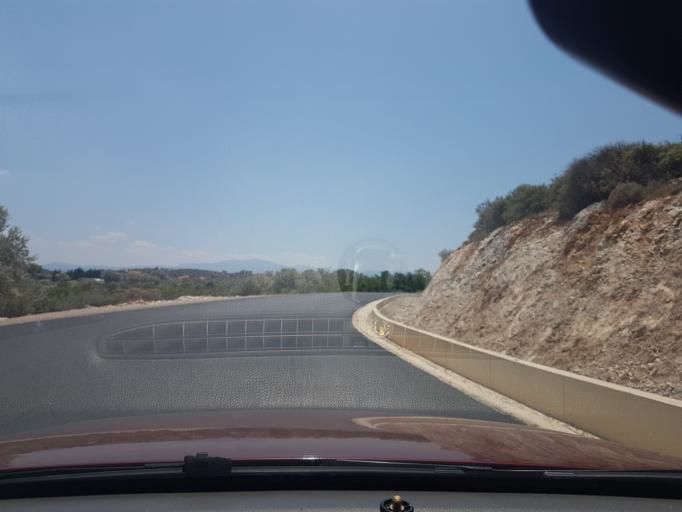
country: GR
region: Central Greece
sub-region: Nomos Evvoias
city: Filla
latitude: 38.4453
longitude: 23.6732
